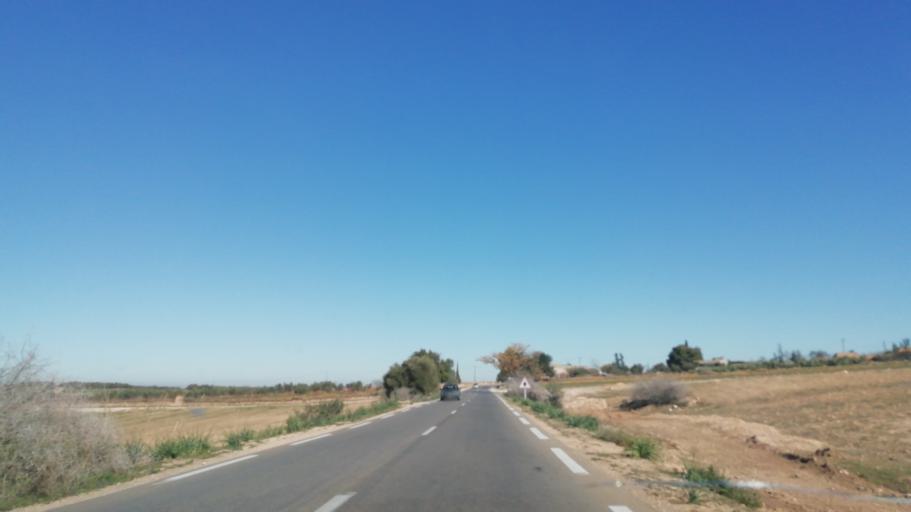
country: DZ
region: Tlemcen
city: Beni Mester
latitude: 34.8217
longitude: -1.6129
